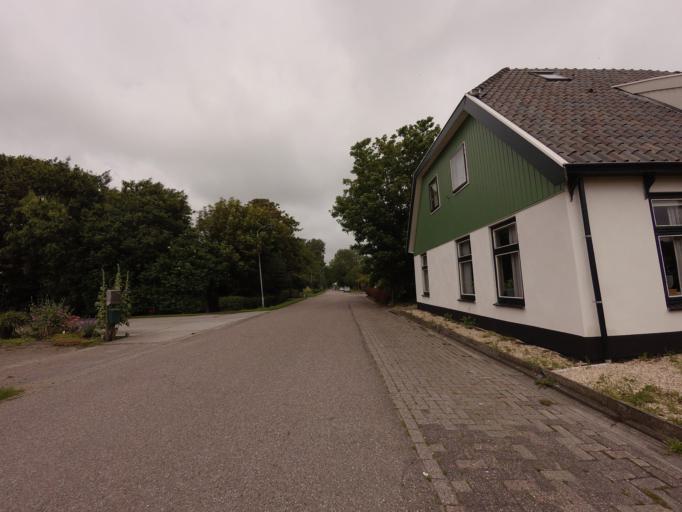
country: NL
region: North Holland
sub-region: Gemeente Schagen
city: Harenkarspel
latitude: 52.7650
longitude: 4.7772
